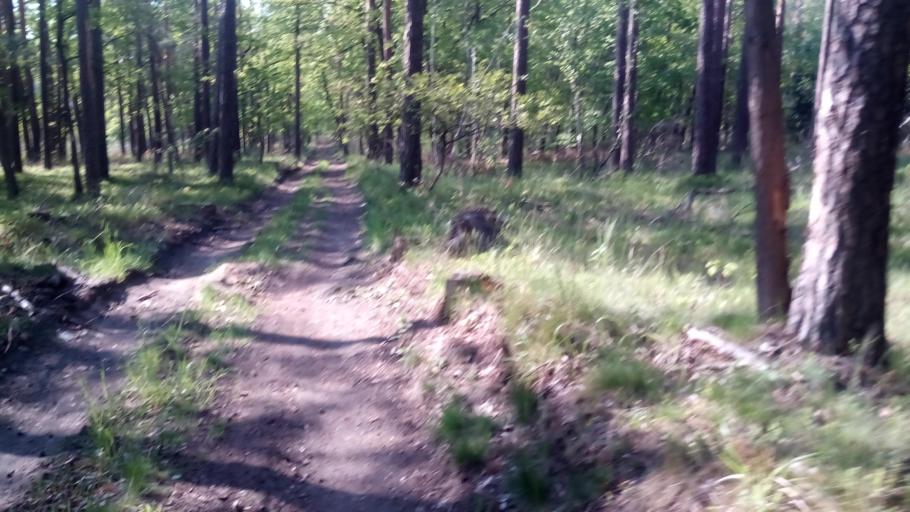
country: PL
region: Opole Voivodeship
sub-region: Powiat opolski
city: Tarnow Opolski
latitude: 50.5851
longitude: 18.0538
